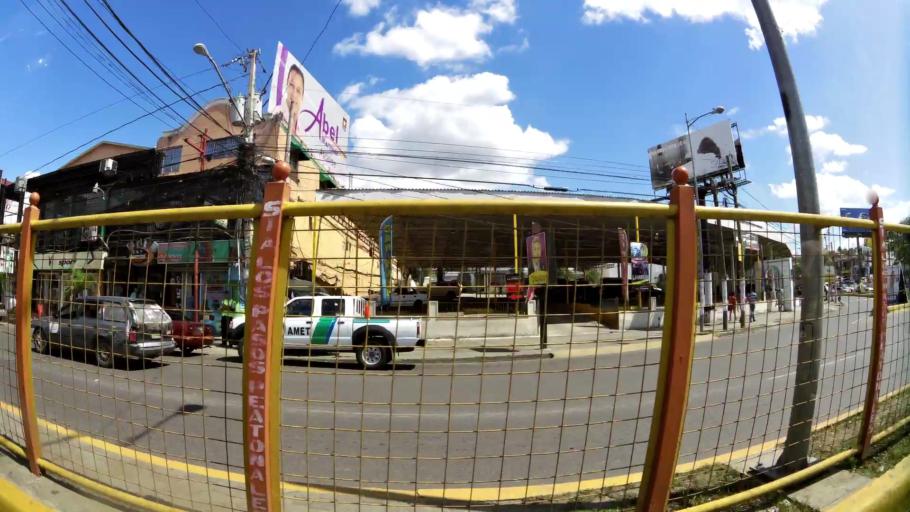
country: DO
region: Santiago
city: Santiago de los Caballeros
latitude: 19.4323
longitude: -70.6926
